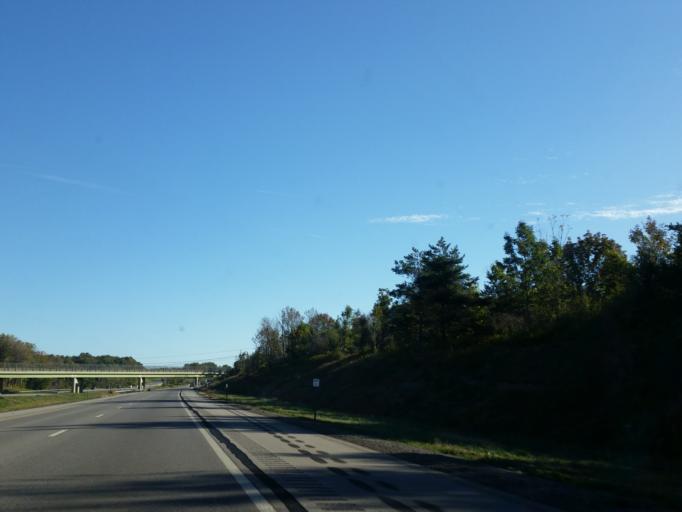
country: US
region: New York
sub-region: Erie County
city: Angola
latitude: 42.6263
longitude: -79.0000
